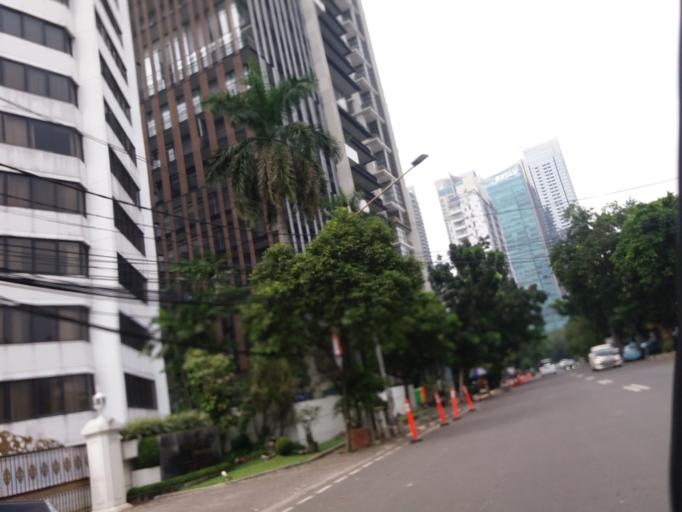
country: ID
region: Jakarta Raya
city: Jakarta
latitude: -6.2293
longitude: 106.8018
